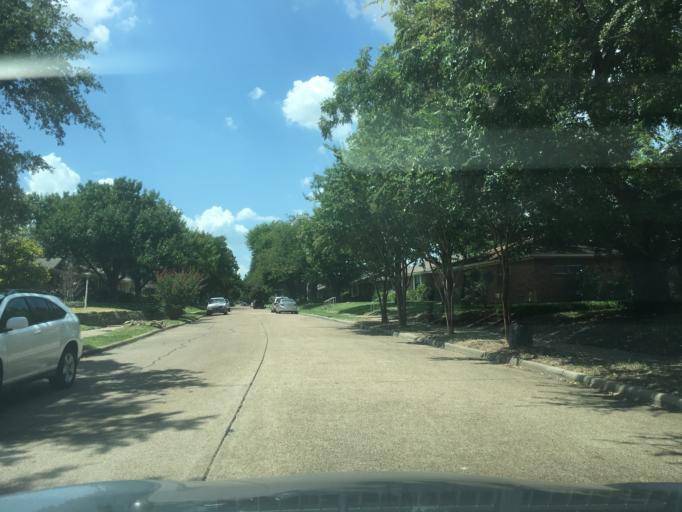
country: US
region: Texas
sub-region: Dallas County
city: Garland
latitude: 32.8703
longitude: -96.6489
